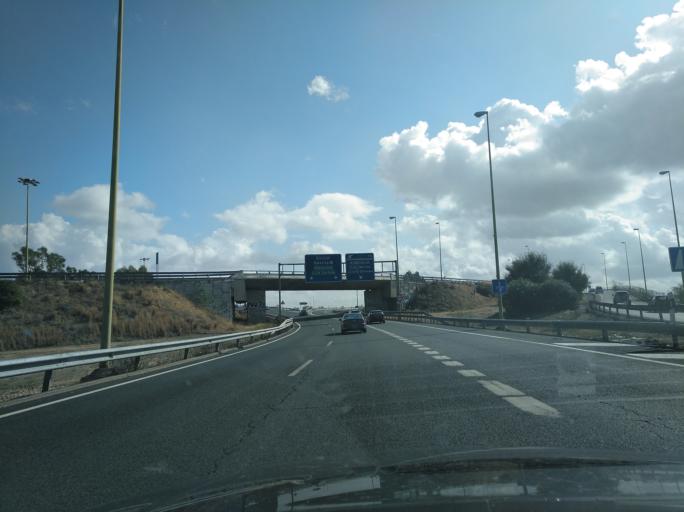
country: ES
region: Andalusia
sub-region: Provincia de Sevilla
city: Camas
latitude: 37.3896
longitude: -6.0292
